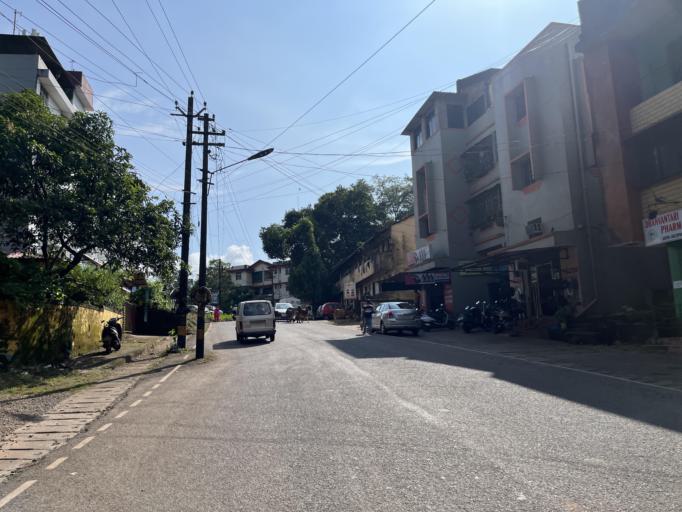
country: IN
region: Goa
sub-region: North Goa
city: Ponda
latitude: 15.3997
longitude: 74.0096
